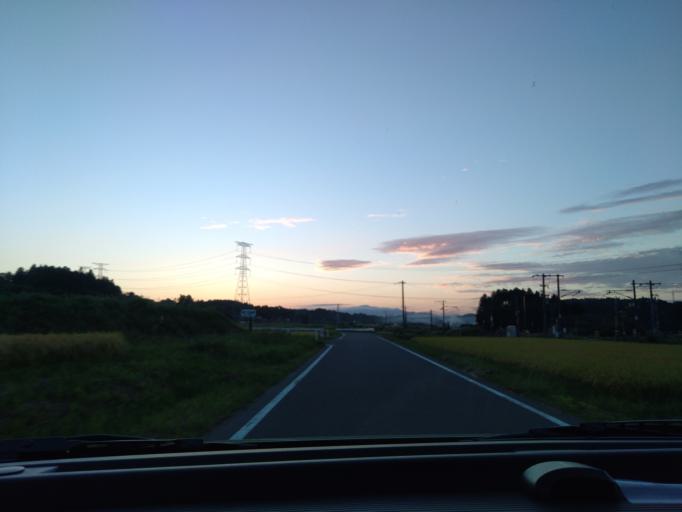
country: JP
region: Iwate
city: Ichinoseki
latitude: 38.8575
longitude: 141.1442
